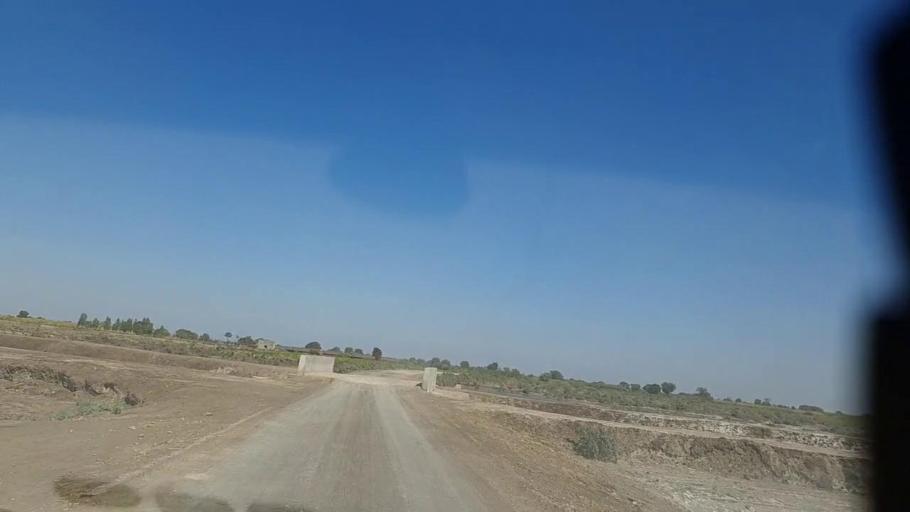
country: PK
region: Sindh
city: Digri
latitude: 25.1661
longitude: 69.0489
